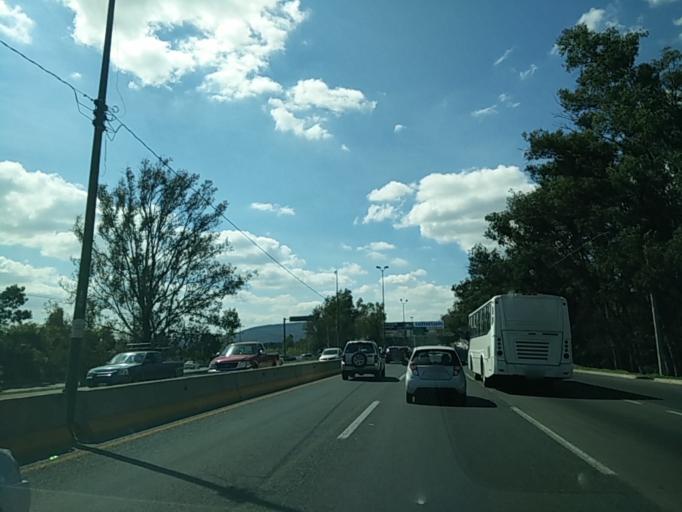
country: MX
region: Jalisco
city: Zapopan2
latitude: 20.7108
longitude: -103.4389
